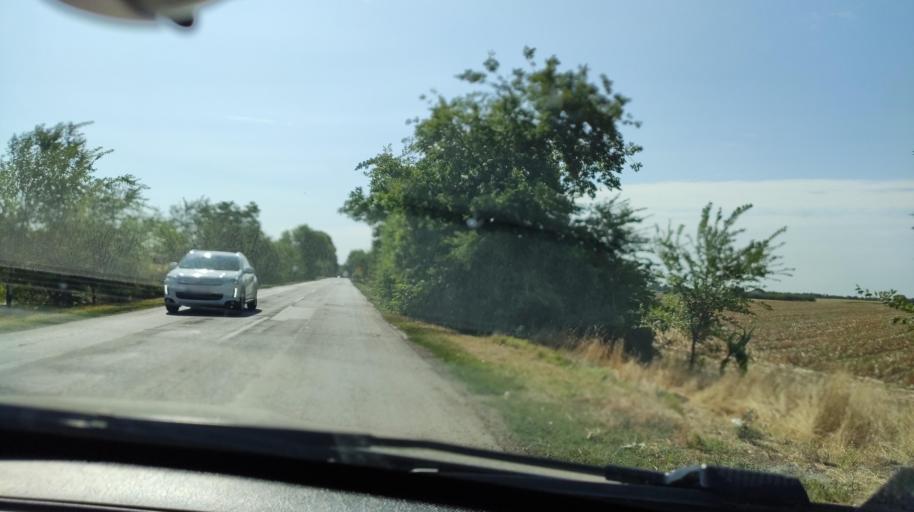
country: RS
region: Autonomna Pokrajina Vojvodina
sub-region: Severnobacki Okrug
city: Backa Topola
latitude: 45.8174
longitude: 19.6139
